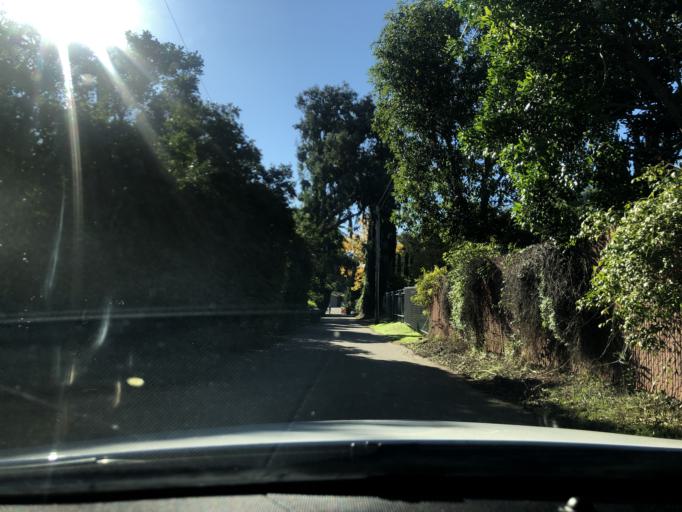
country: US
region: California
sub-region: San Diego County
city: Rancho San Diego
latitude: 32.7681
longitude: -116.9386
